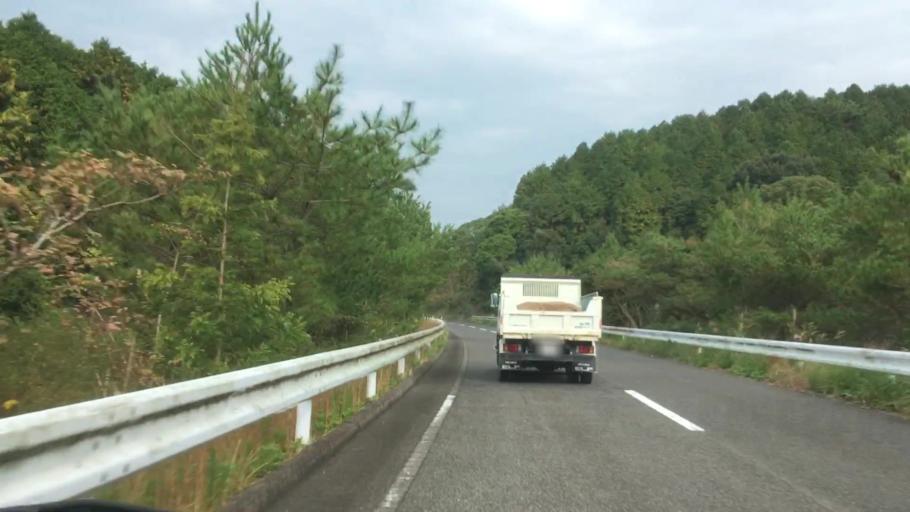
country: JP
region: Nagasaki
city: Sasebo
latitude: 33.0242
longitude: 129.6978
